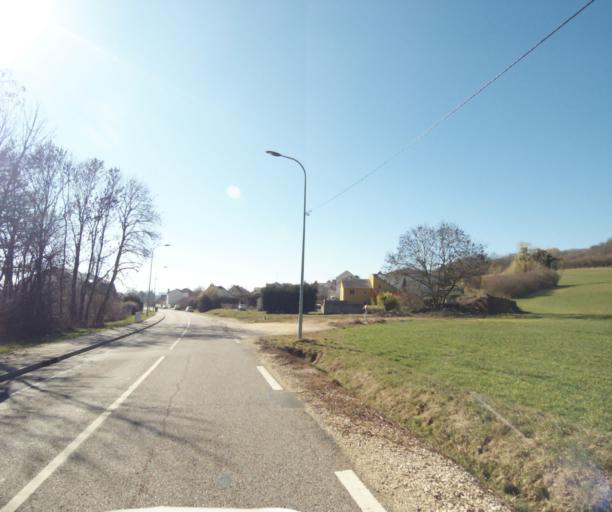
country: FR
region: Lorraine
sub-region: Departement de Meurthe-et-Moselle
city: Essey-les-Nancy
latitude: 48.7115
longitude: 6.2381
